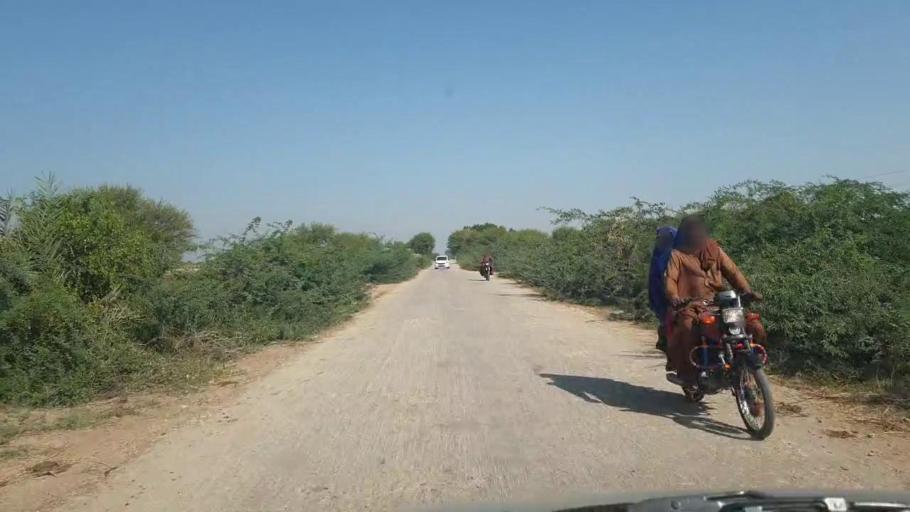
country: PK
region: Sindh
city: Tando Bago
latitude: 24.8188
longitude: 68.9846
